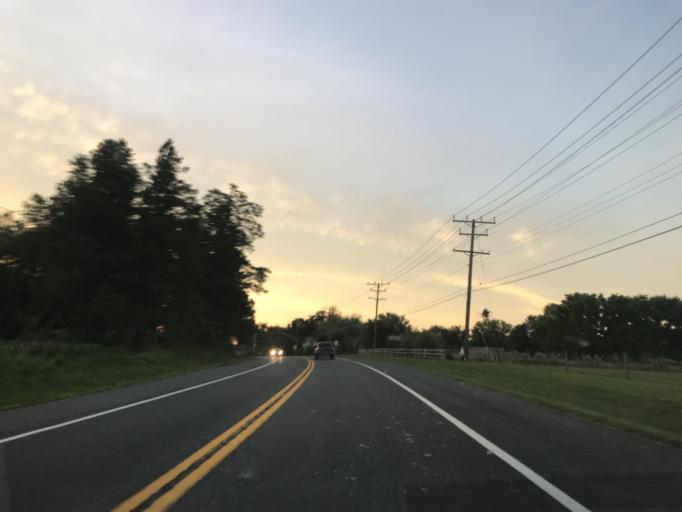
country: US
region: Maryland
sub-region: Harford County
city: Riverside
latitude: 39.5505
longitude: -76.2365
